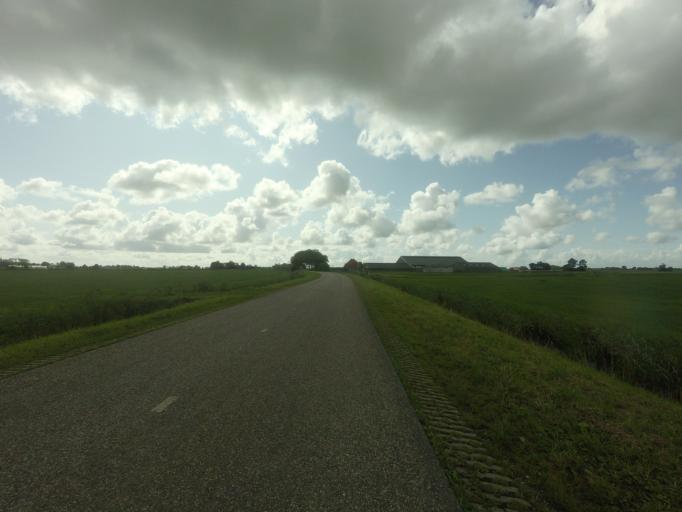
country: NL
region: Friesland
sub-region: Sudwest Fryslan
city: IJlst
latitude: 53.0556
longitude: 5.6151
